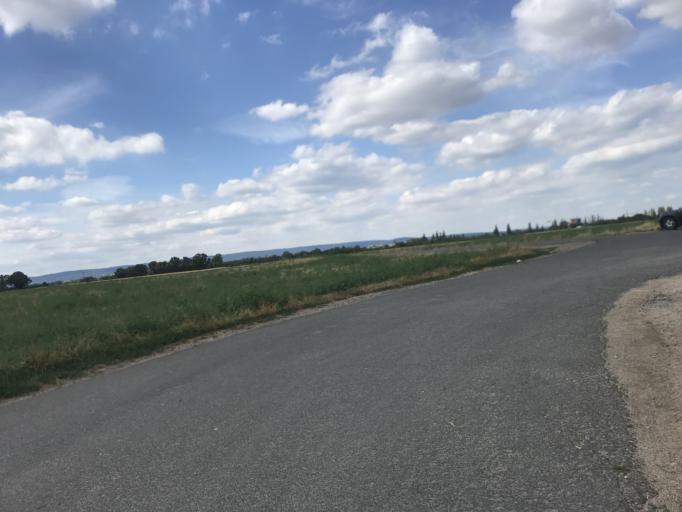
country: DE
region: Hesse
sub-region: Regierungsbezirk Darmstadt
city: Wiesbaden
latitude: 50.0427
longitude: 8.2945
